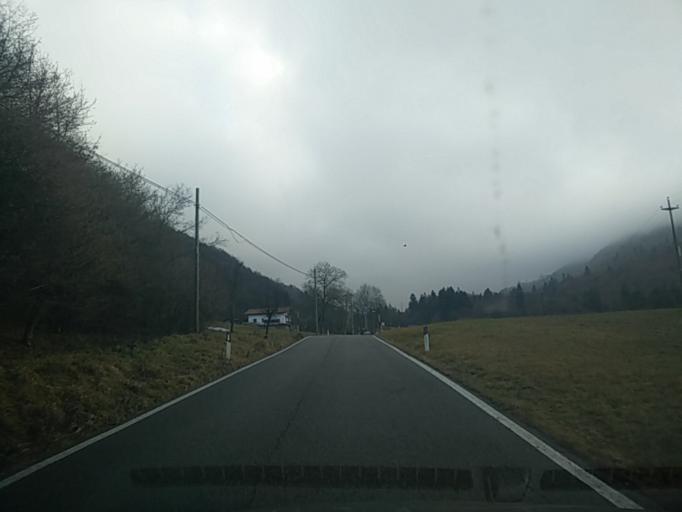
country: IT
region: Veneto
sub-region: Provincia di Treviso
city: Cison di Valmarino
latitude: 46.0234
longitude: 12.1626
